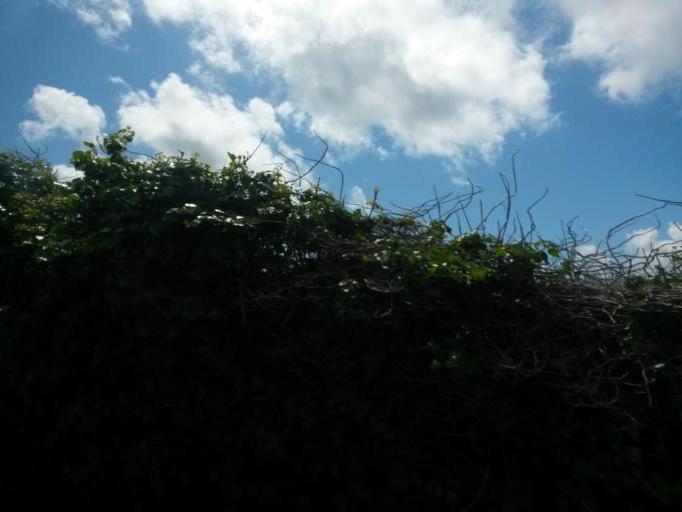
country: IE
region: Munster
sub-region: Waterford
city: Dunmore East
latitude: 52.1952
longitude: -6.8988
